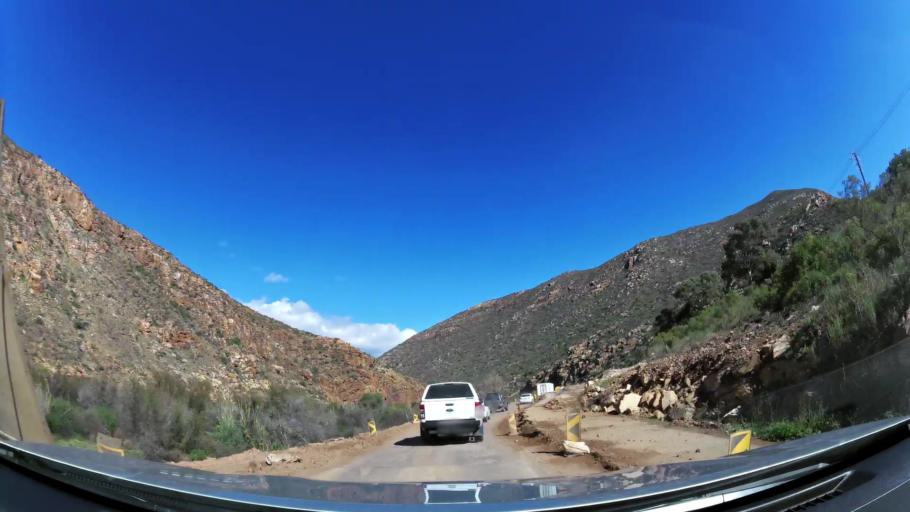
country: ZA
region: Western Cape
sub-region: Cape Winelands District Municipality
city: Ashton
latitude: -33.8114
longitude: 20.0930
